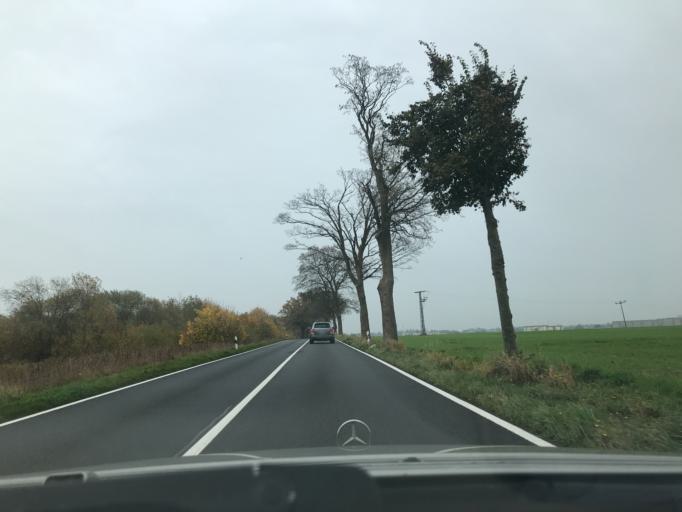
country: DE
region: Mecklenburg-Vorpommern
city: Wolgast
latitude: 54.0671
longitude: 13.7599
